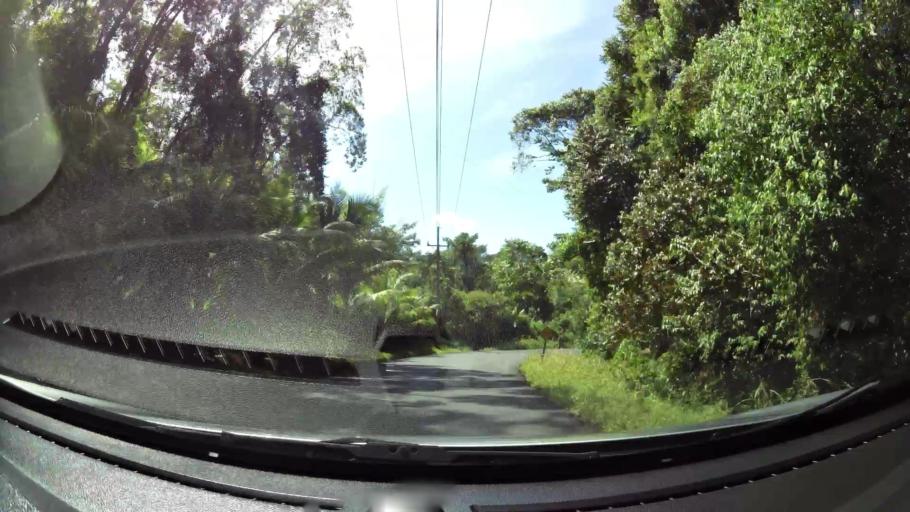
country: CR
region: San Jose
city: San Isidro
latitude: 9.2799
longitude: -83.8302
